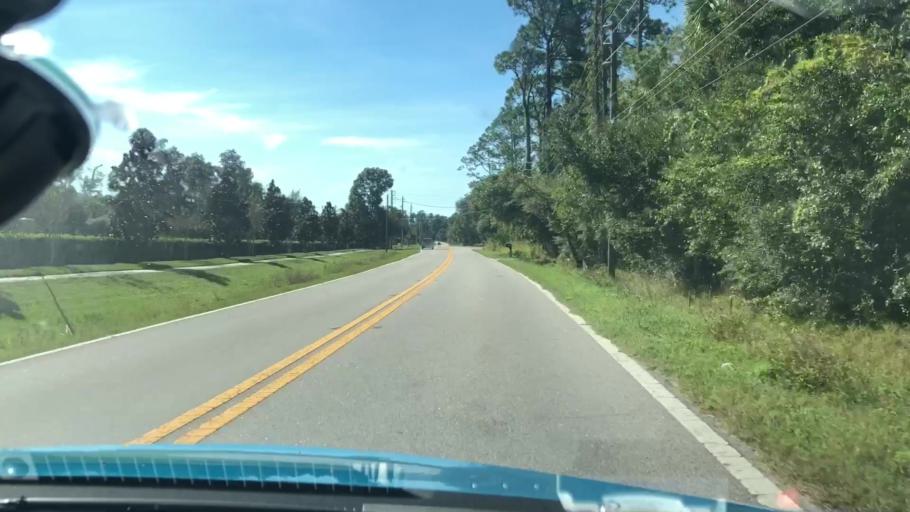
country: US
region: Florida
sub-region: Seminole County
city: Heathrow
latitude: 28.8238
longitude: -81.3576
